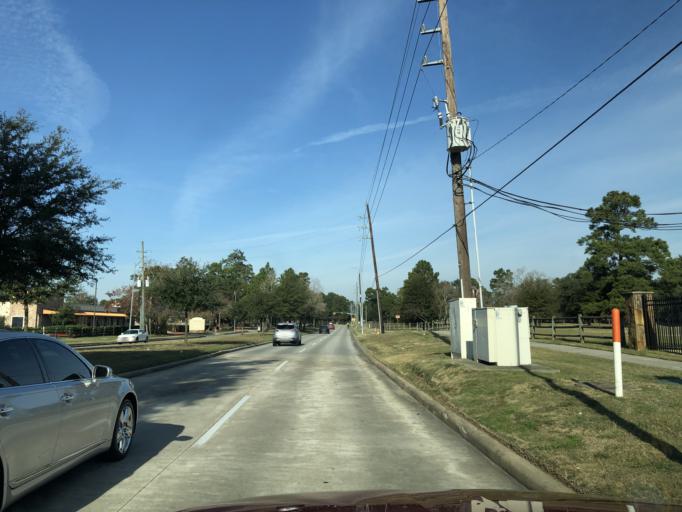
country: US
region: Texas
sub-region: Harris County
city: Tomball
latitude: 30.0351
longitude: -95.5590
